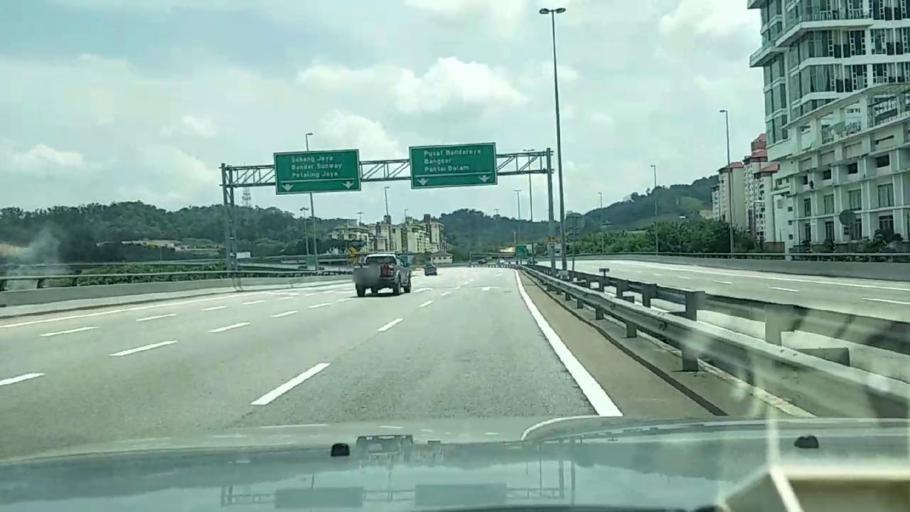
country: MY
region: Kuala Lumpur
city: Kuala Lumpur
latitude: 3.0939
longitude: 101.6743
